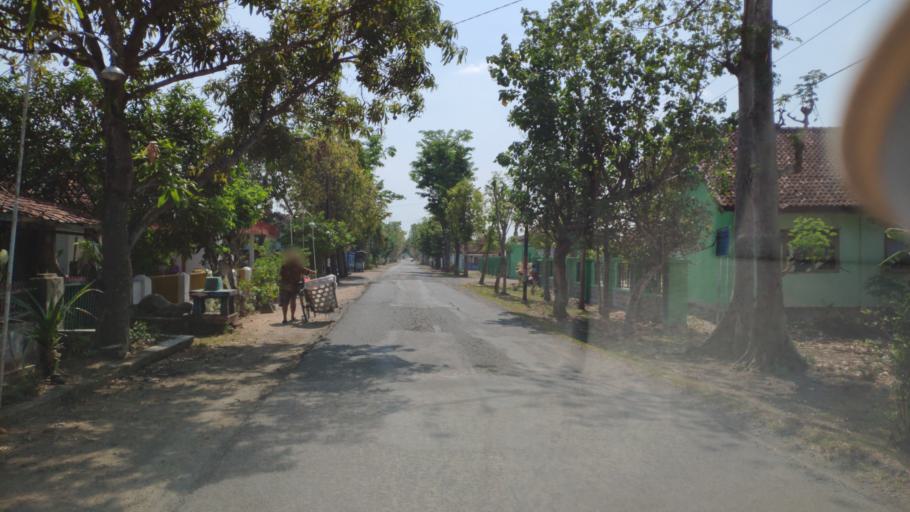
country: ID
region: Central Java
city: Kedungjenar
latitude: -6.9799
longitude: 111.4232
